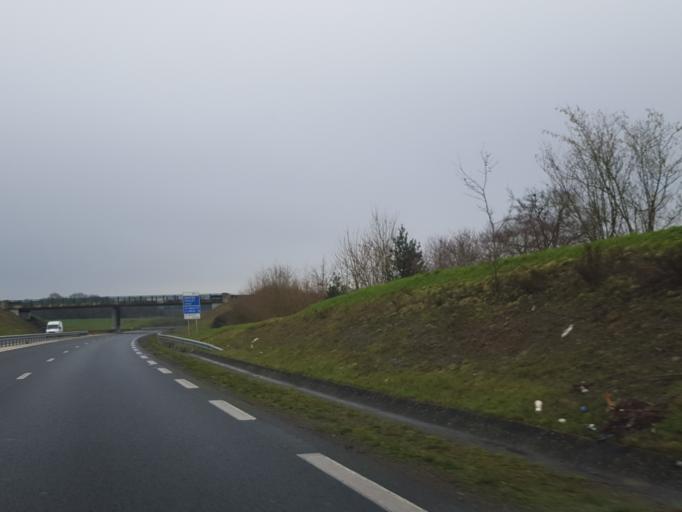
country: FR
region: Pays de la Loire
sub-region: Departement de la Vendee
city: Dompierre-sur-Yon
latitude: 46.6789
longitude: -1.3725
